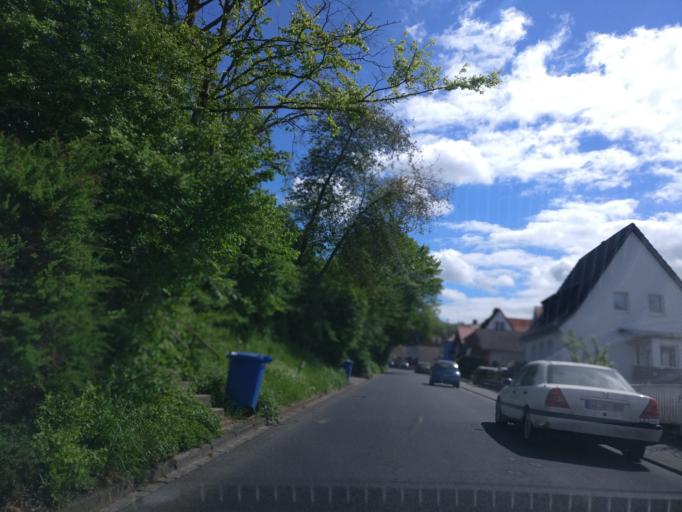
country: DE
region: Lower Saxony
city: Hannoversch Munden
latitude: 51.4070
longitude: 9.6587
